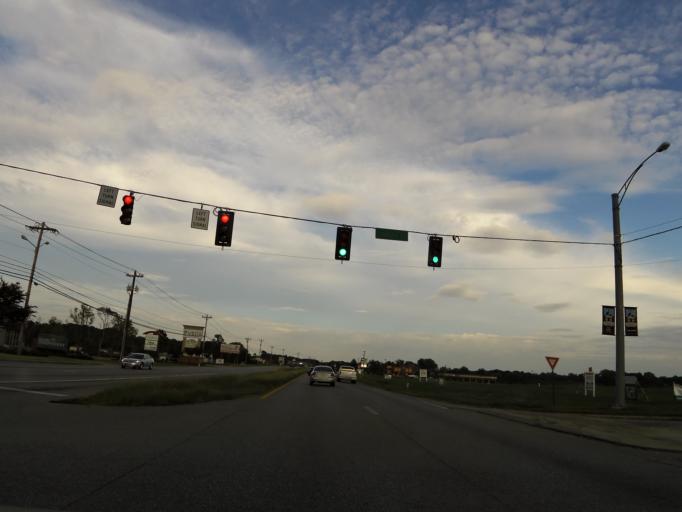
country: US
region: Alabama
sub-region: Limestone County
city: Athens
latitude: 34.7813
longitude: -86.9307
